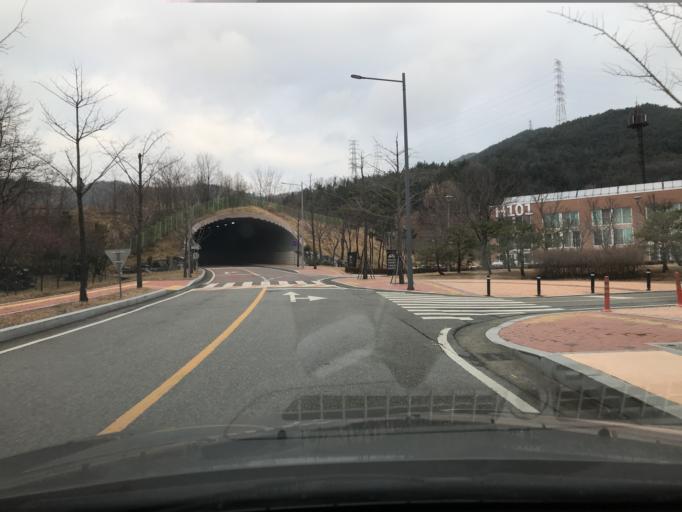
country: KR
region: Daegu
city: Hwawon
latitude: 35.7038
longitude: 128.4612
